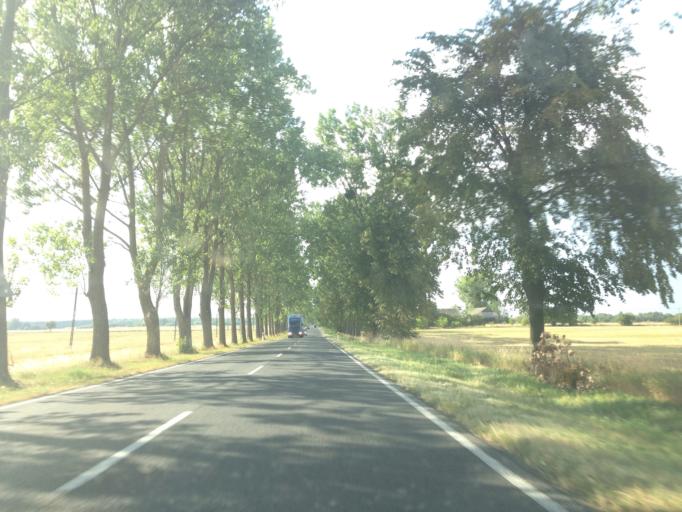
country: PL
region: Kujawsko-Pomorskie
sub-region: Powiat swiecki
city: Bukowiec
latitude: 53.4561
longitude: 18.1990
